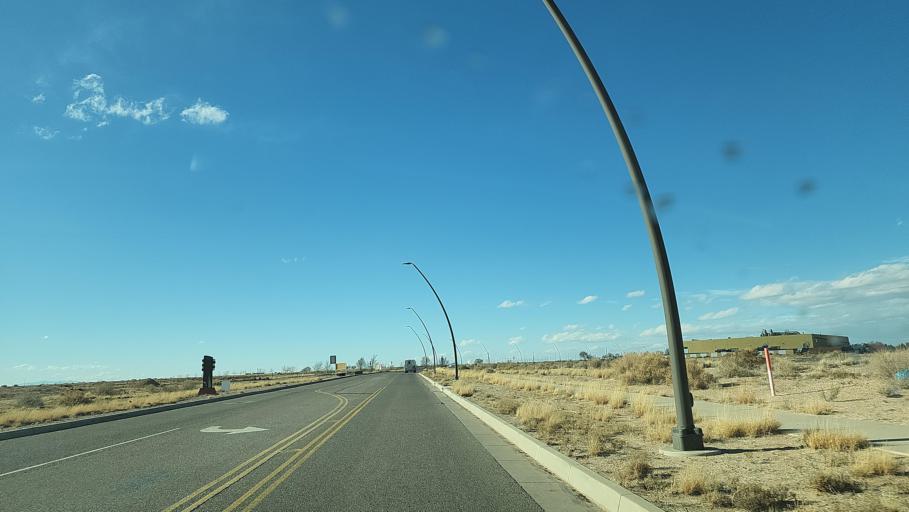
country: US
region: New Mexico
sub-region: Bernalillo County
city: South Valley
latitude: 34.9925
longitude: -106.6199
